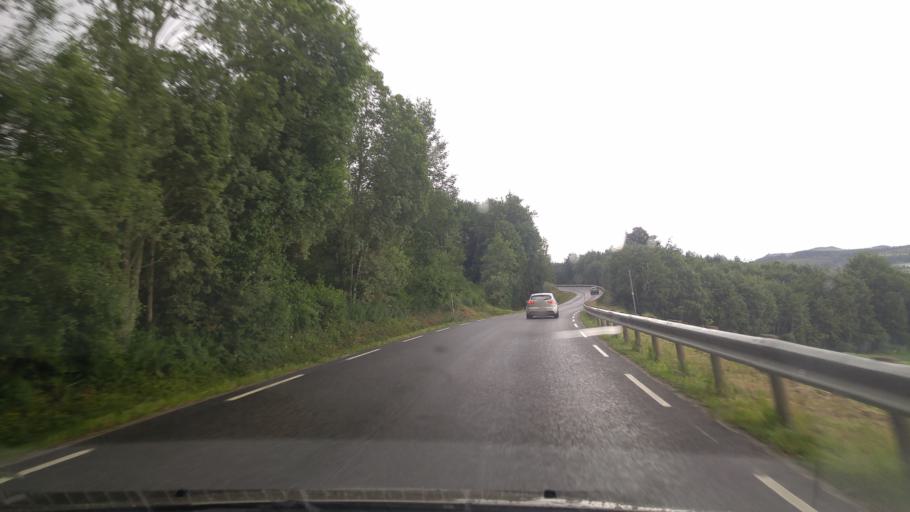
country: NO
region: Nord-Trondelag
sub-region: Levanger
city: Skogn
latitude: 63.6723
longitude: 11.2374
